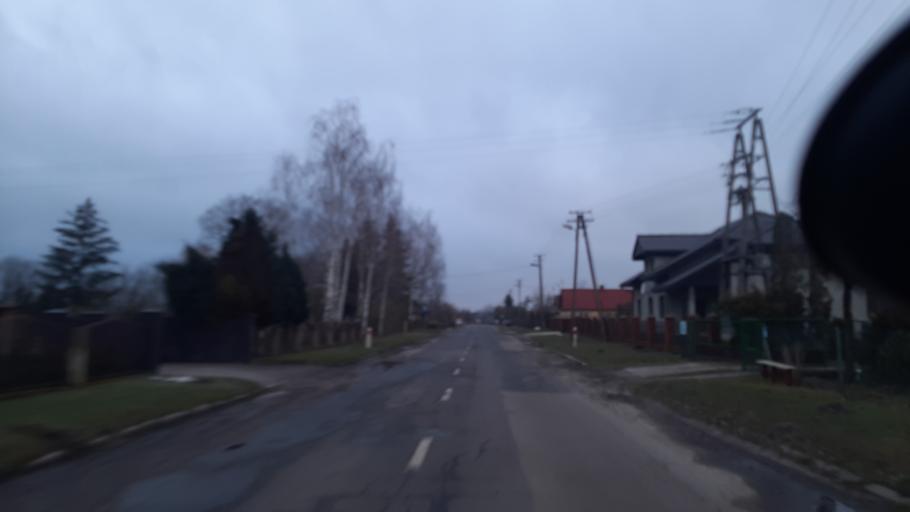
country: PL
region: Lublin Voivodeship
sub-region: Powiat parczewski
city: Debowa Kloda
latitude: 51.6199
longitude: 23.0932
